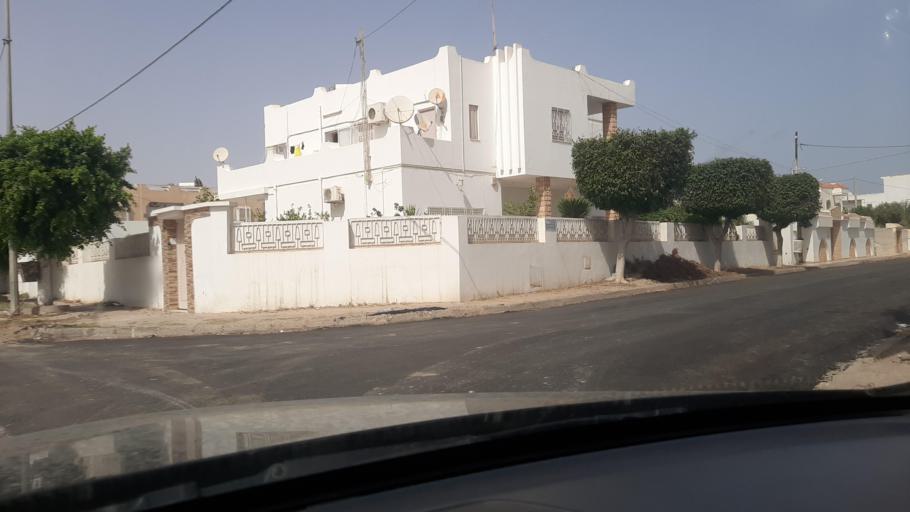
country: TN
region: Safaqis
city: Sfax
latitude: 34.7601
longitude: 10.7556
